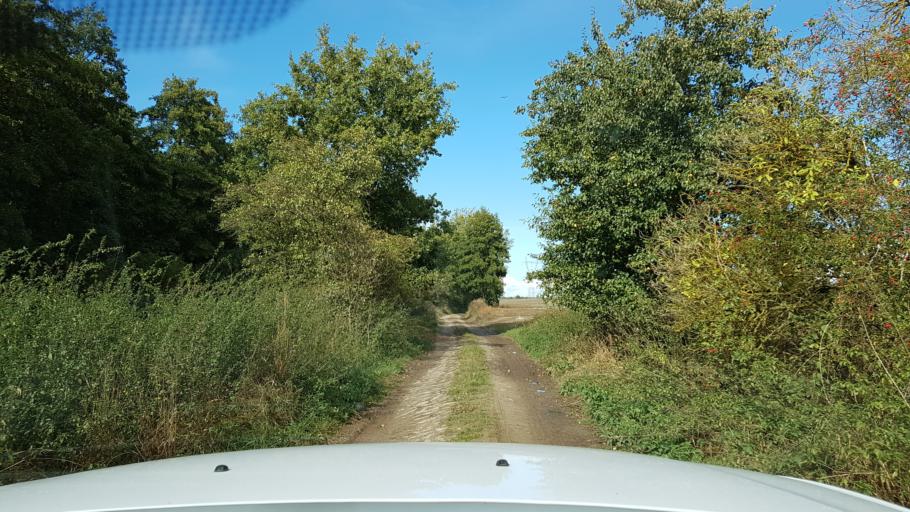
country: PL
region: West Pomeranian Voivodeship
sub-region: Powiat gryfinski
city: Banie
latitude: 53.1217
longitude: 14.6492
